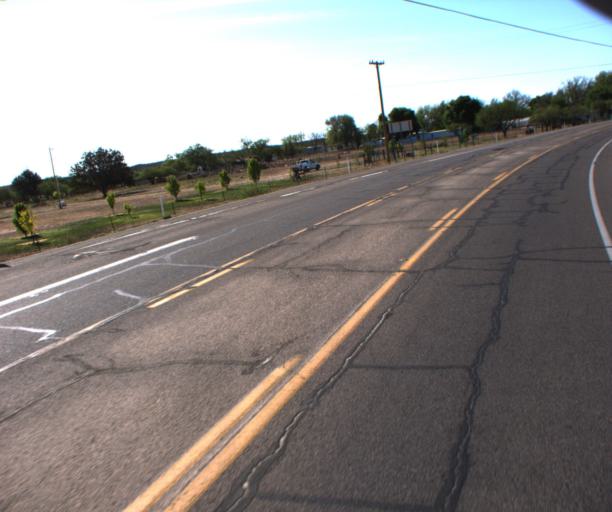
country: US
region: Arizona
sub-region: Cochise County
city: Saint David
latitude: 31.9035
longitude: -110.2138
